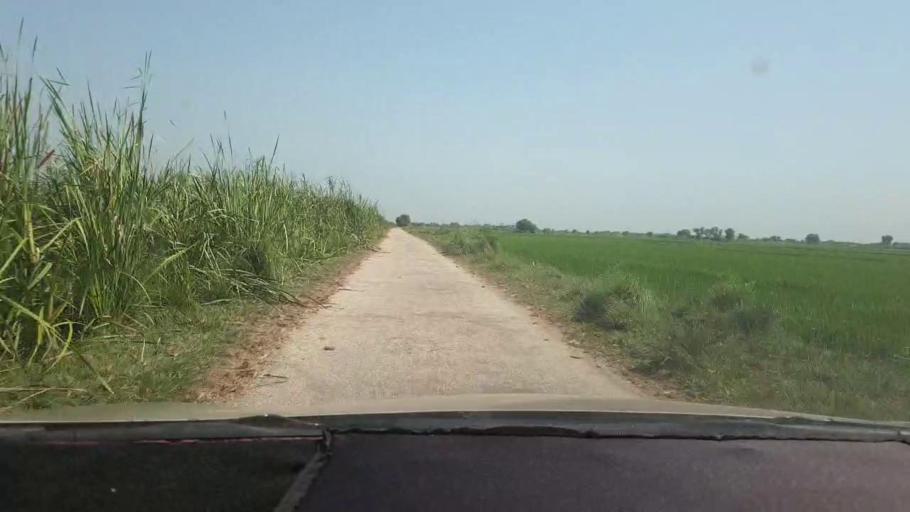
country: PK
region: Sindh
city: Miro Khan
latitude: 27.7007
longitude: 68.0911
